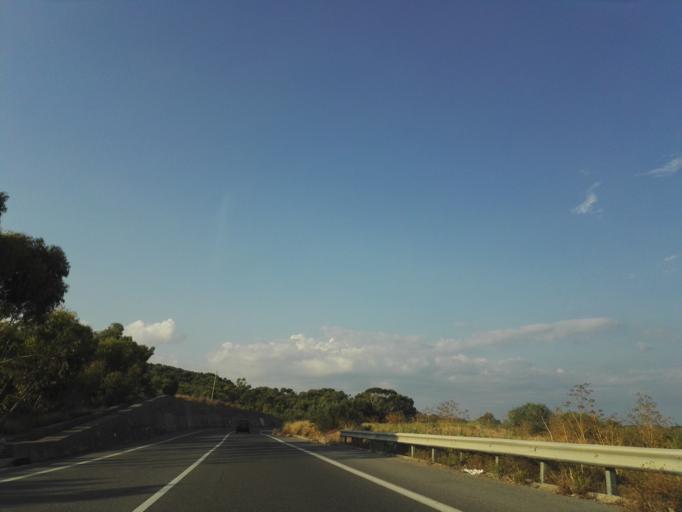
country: IT
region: Calabria
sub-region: Provincia di Reggio Calabria
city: Riace Marina
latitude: 38.3688
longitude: 16.5023
